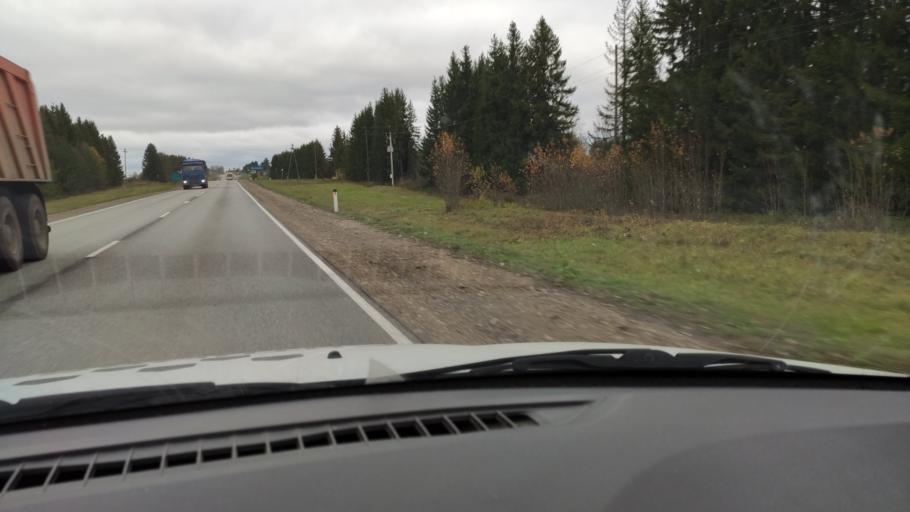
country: RU
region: Kirov
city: Slobodskoy
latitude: 58.7391
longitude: 50.2953
